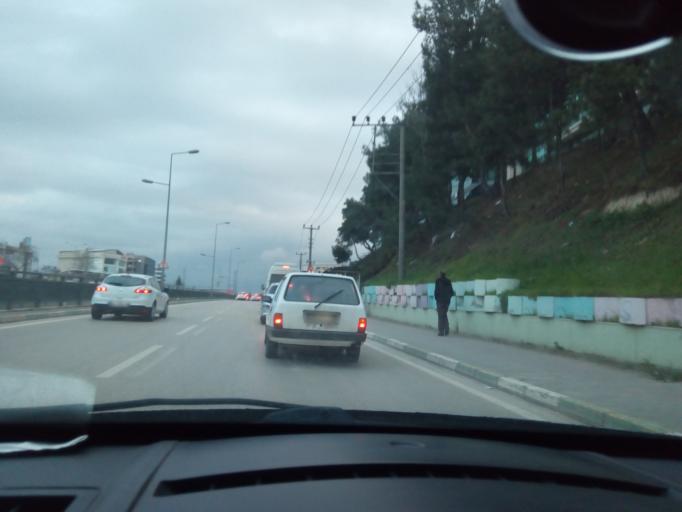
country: TR
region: Bursa
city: Yildirim
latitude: 40.2324
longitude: 28.9814
